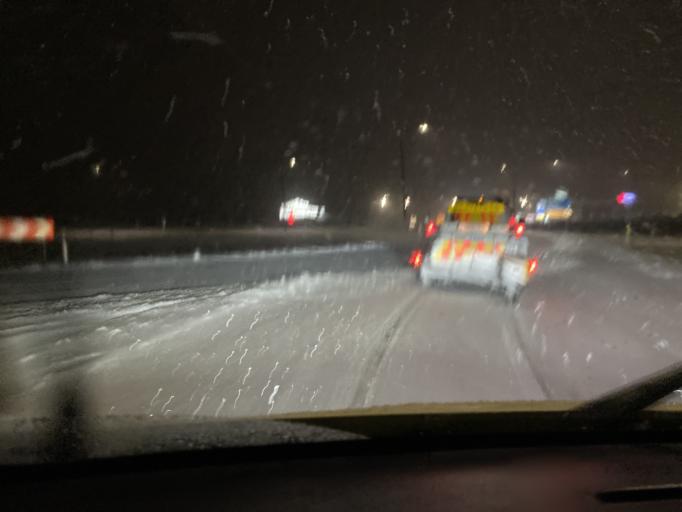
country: EE
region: Harju
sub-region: Kuusalu vald
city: Kuusalu
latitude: 59.4460
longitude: 25.3756
